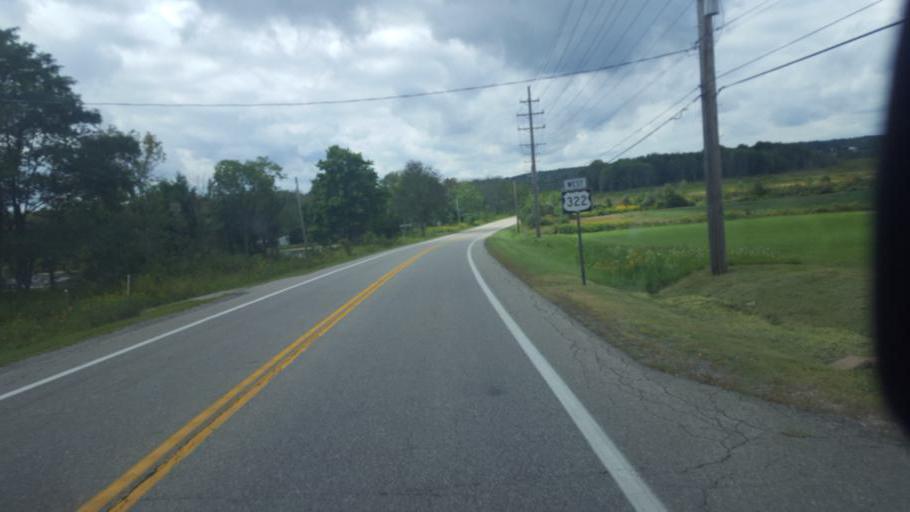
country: US
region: Ohio
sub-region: Geauga County
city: Burton
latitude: 41.5321
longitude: -81.1638
